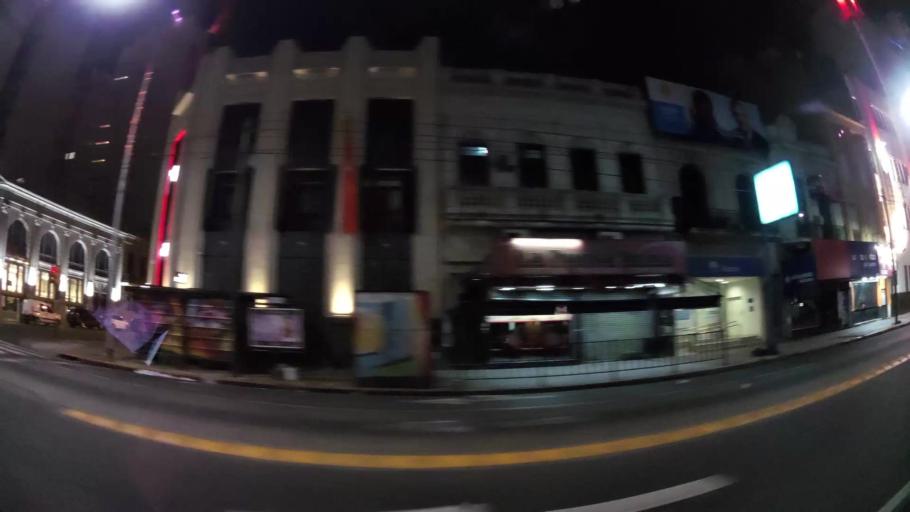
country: AR
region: Buenos Aires
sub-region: Partido de Avellaneda
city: Avellaneda
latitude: -34.6597
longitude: -58.3683
